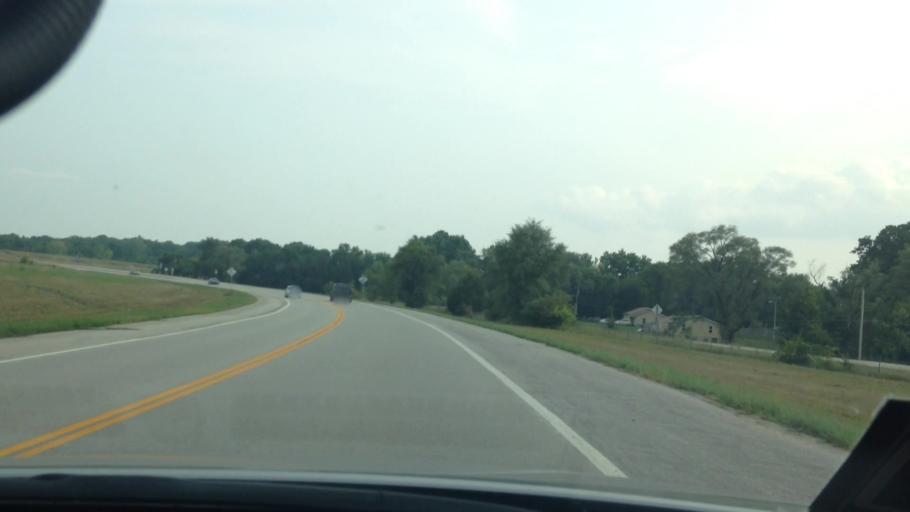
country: US
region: Kansas
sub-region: Leavenworth County
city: Lansing
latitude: 39.1845
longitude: -94.8029
